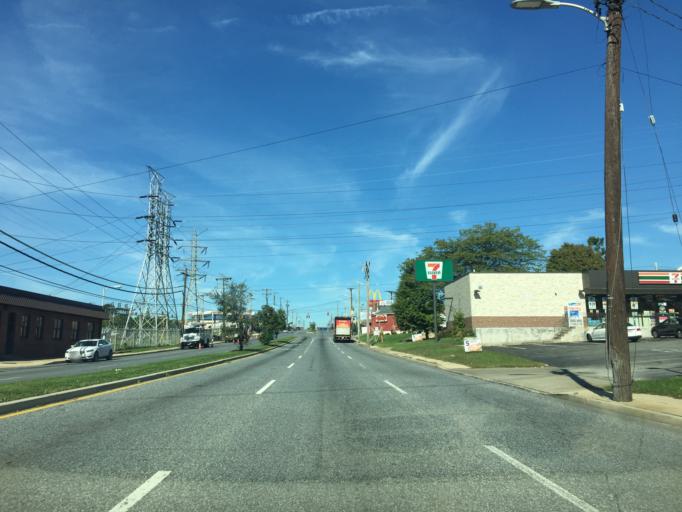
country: US
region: Maryland
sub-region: Baltimore County
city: Rosedale
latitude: 39.3080
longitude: -76.5608
